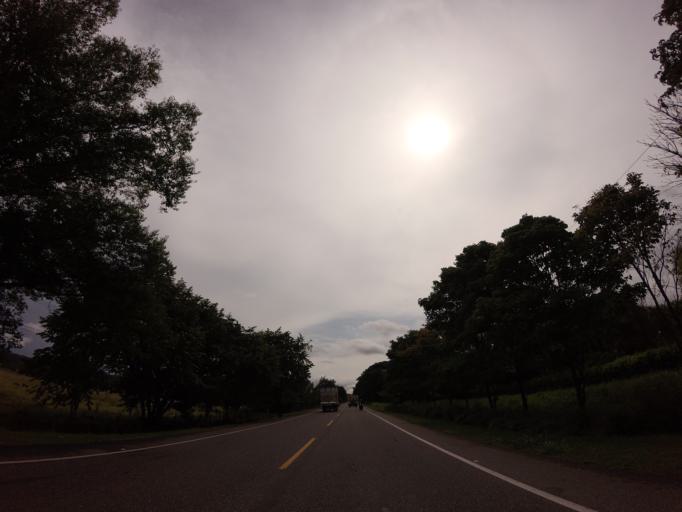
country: CO
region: Caldas
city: La Dorada
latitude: 5.4012
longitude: -74.6960
